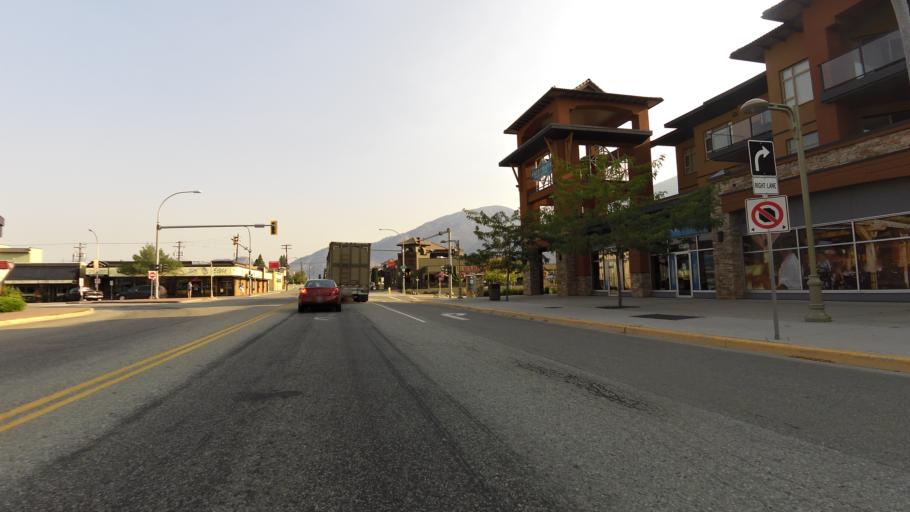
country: CA
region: British Columbia
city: Osoyoos
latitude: 49.0325
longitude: -119.4634
